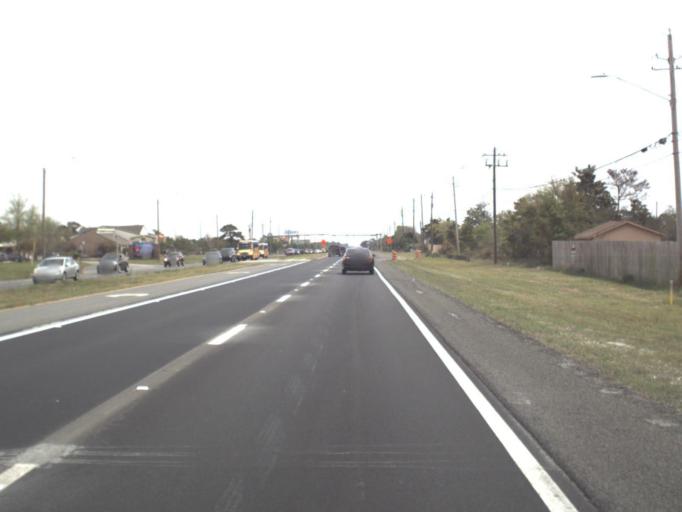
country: US
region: Florida
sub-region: Santa Rosa County
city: Holley
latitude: 30.4019
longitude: -86.9090
